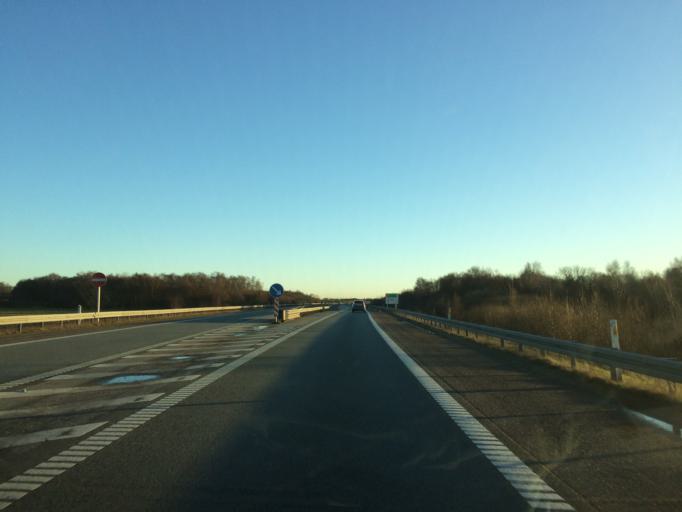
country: DK
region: Central Jutland
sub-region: Herning Kommune
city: Herning
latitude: 56.1643
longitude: 9.0025
